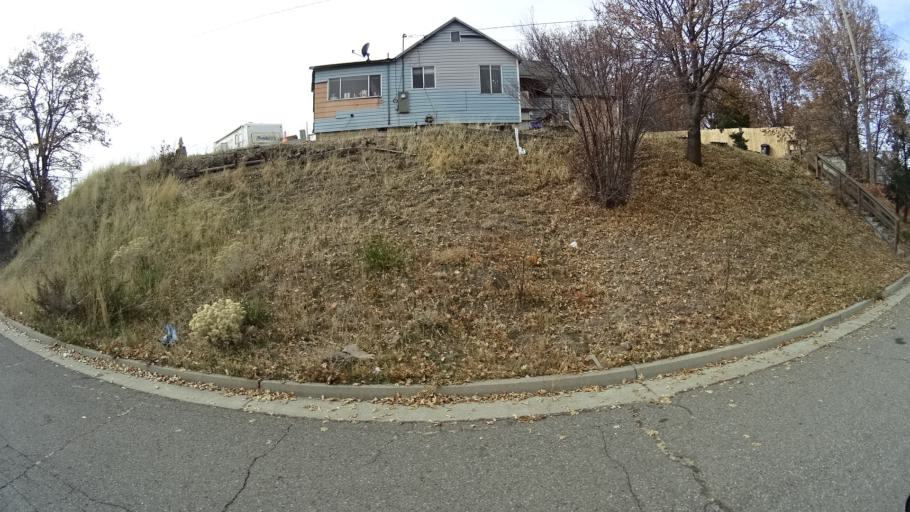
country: US
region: California
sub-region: Siskiyou County
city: Weed
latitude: 41.4340
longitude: -122.3856
